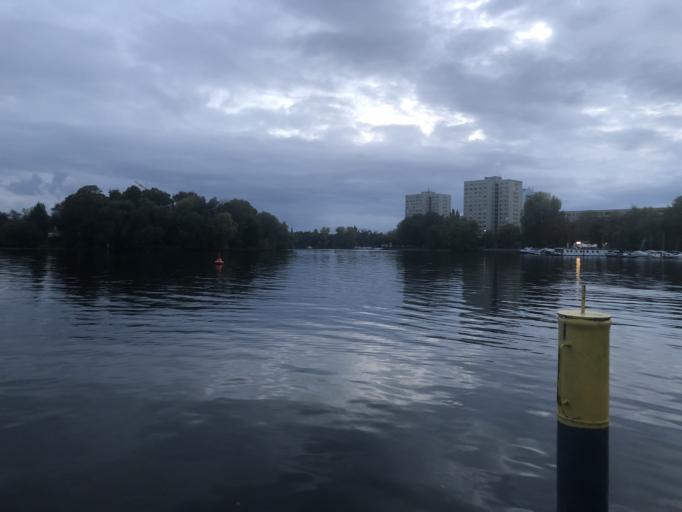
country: DE
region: Brandenburg
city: Potsdam
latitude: 52.3927
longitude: 13.0461
